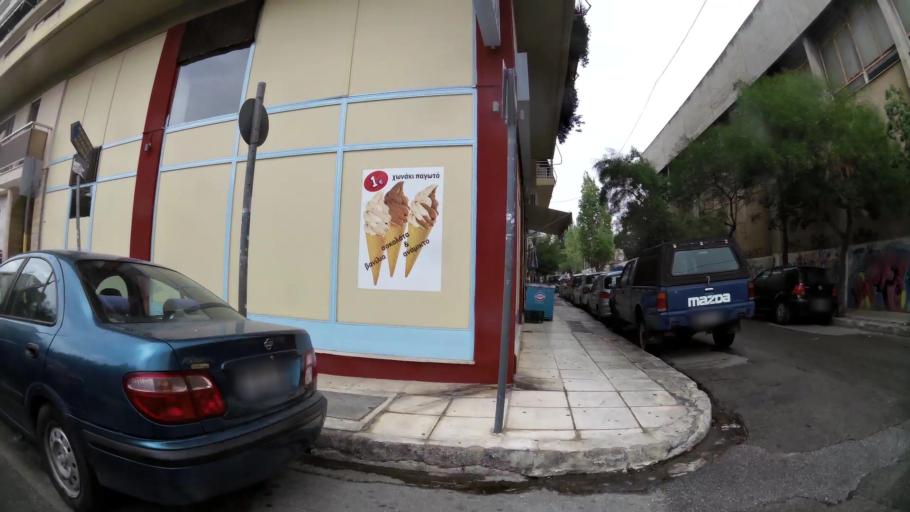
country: GR
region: Attica
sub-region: Nomarchia Athinas
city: Kaisariani
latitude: 37.9665
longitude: 23.7614
